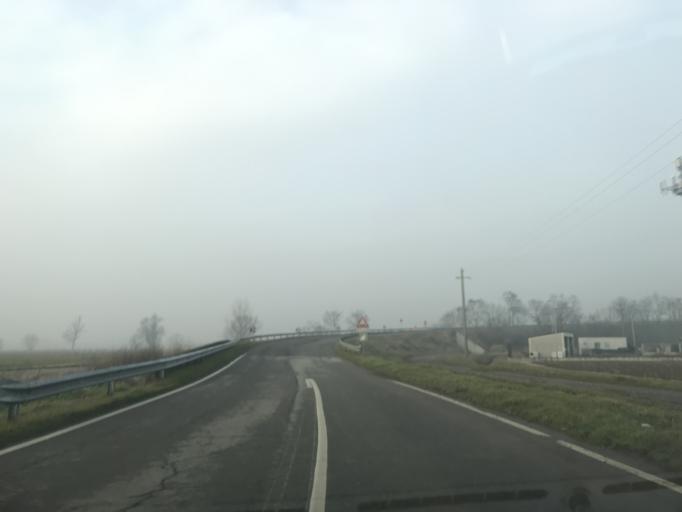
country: IT
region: Lombardy
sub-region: Provincia di Lodi
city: Villanova del Sillaro
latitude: 45.2441
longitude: 9.4873
